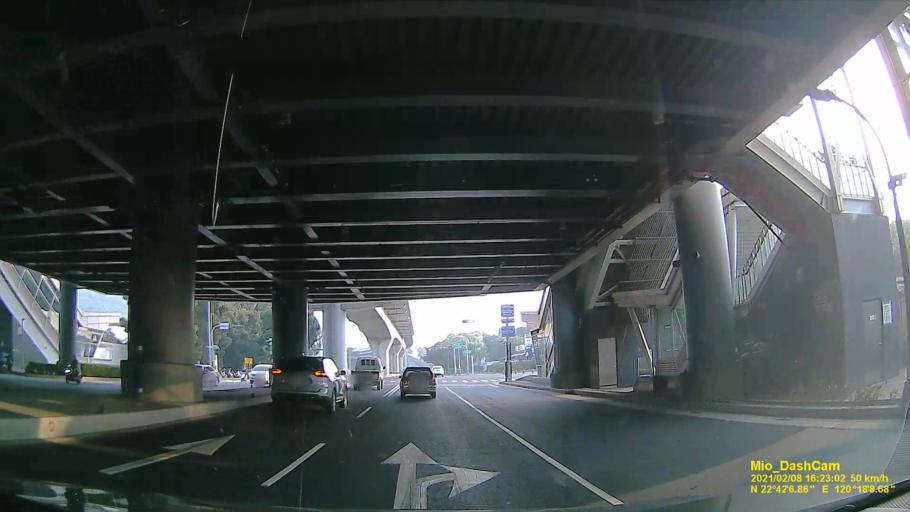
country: TW
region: Kaohsiung
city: Kaohsiung
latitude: 22.7018
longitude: 120.3024
